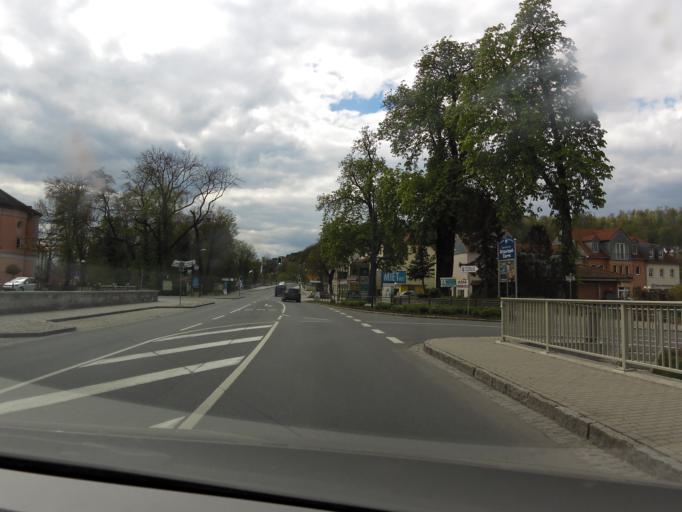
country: DE
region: Saxony-Anhalt
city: Bad Kosen
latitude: 51.1377
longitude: 11.7220
